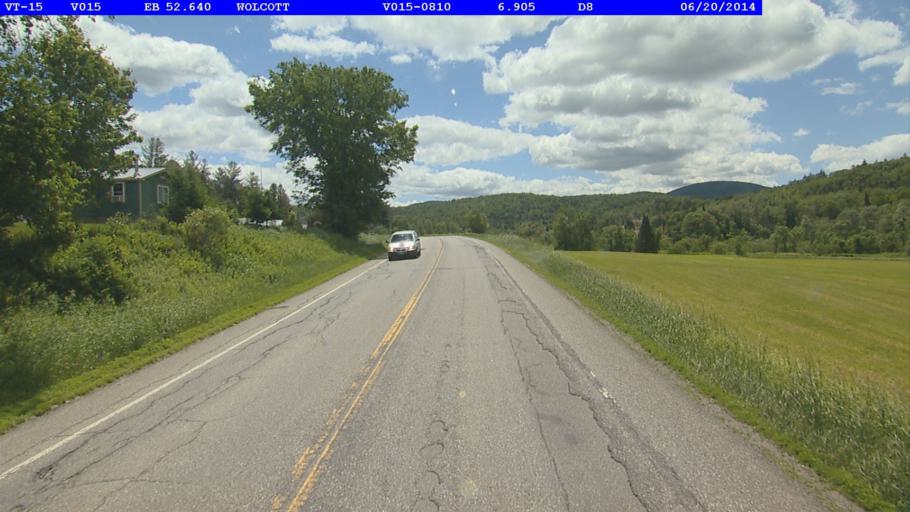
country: US
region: Vermont
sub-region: Caledonia County
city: Hardwick
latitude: 44.5265
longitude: -72.4202
